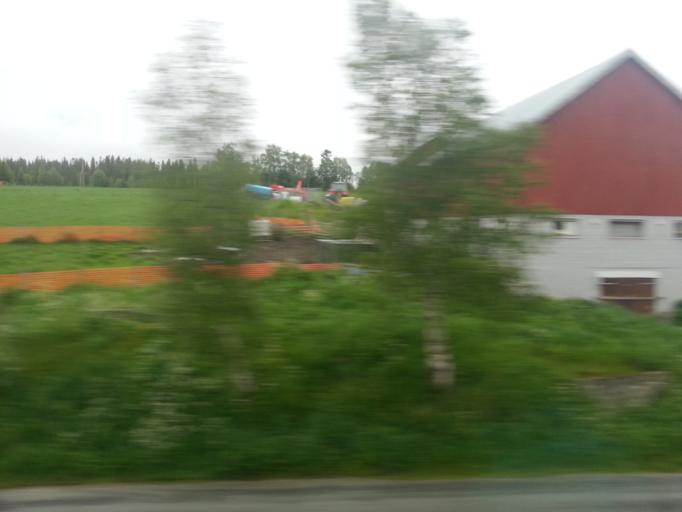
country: NO
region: Sor-Trondelag
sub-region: Rennebu
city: Berkak
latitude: 62.8176
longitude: 10.0206
